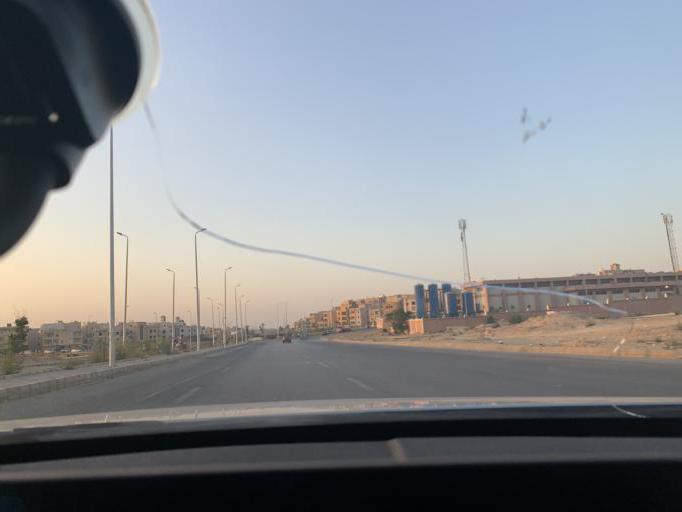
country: EG
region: Muhafazat al Qahirah
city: Cairo
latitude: 29.9971
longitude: 31.4689
